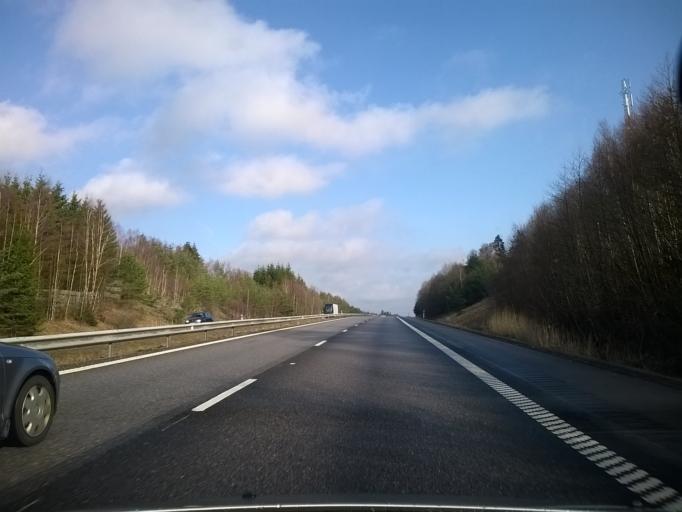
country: SE
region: Vaestra Goetaland
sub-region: Stenungsunds Kommun
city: Stenungsund
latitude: 58.0805
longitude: 11.8863
